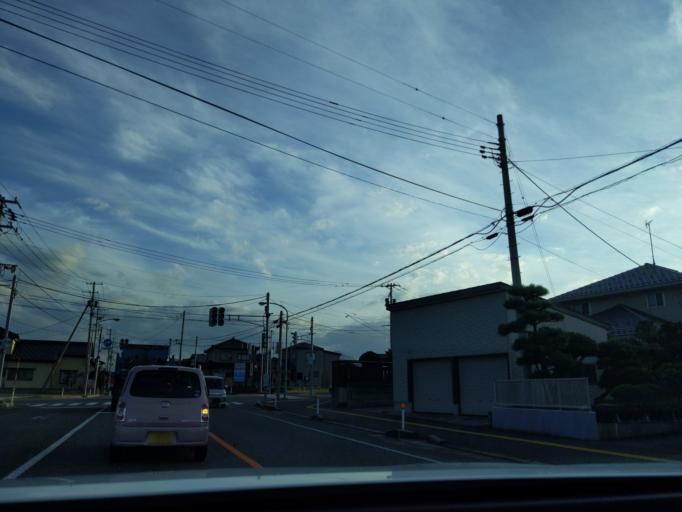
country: JP
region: Niigata
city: Kashiwazaki
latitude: 37.3846
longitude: 138.5691
